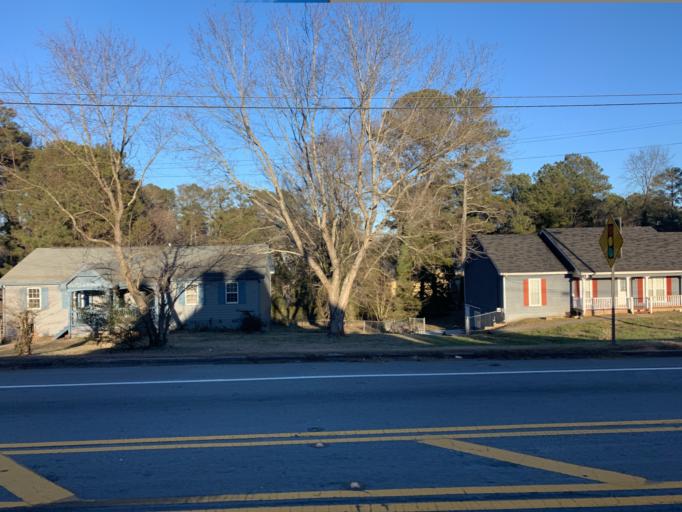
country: US
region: Georgia
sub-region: Gwinnett County
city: Mountain Park
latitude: 33.8730
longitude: -84.1049
